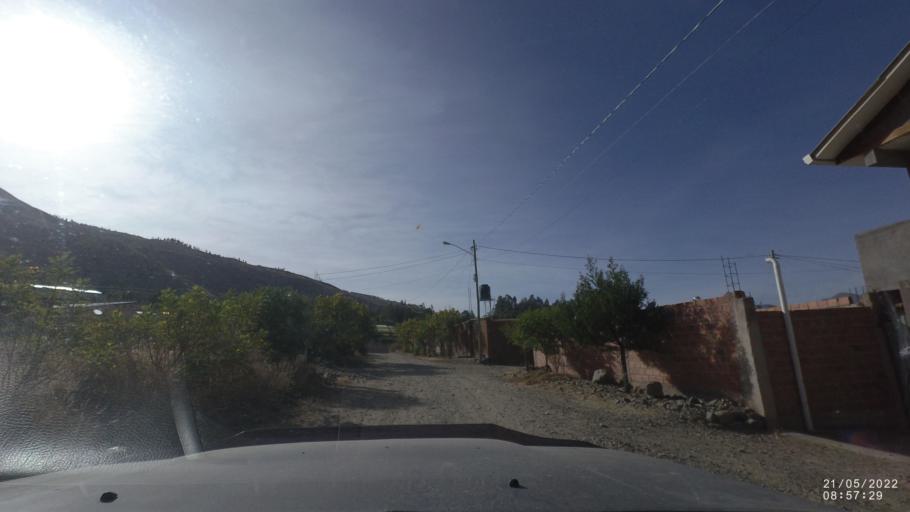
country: BO
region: Cochabamba
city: Cochabamba
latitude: -17.3785
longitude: -66.0395
